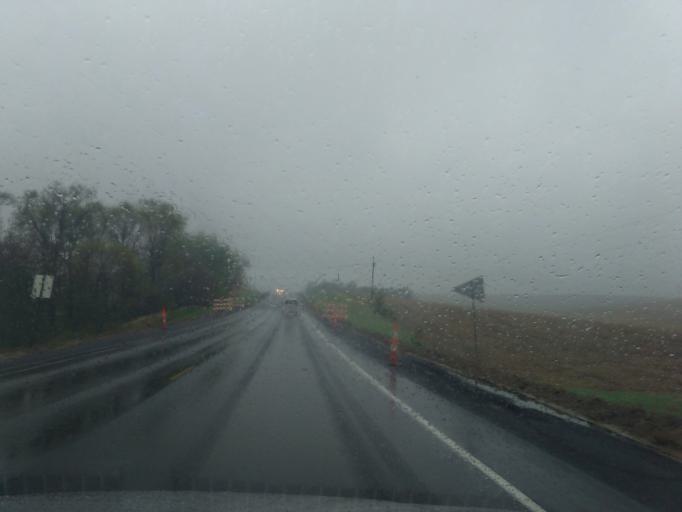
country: US
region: Nebraska
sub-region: Wayne County
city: Wayne
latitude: 42.2056
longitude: -97.1738
